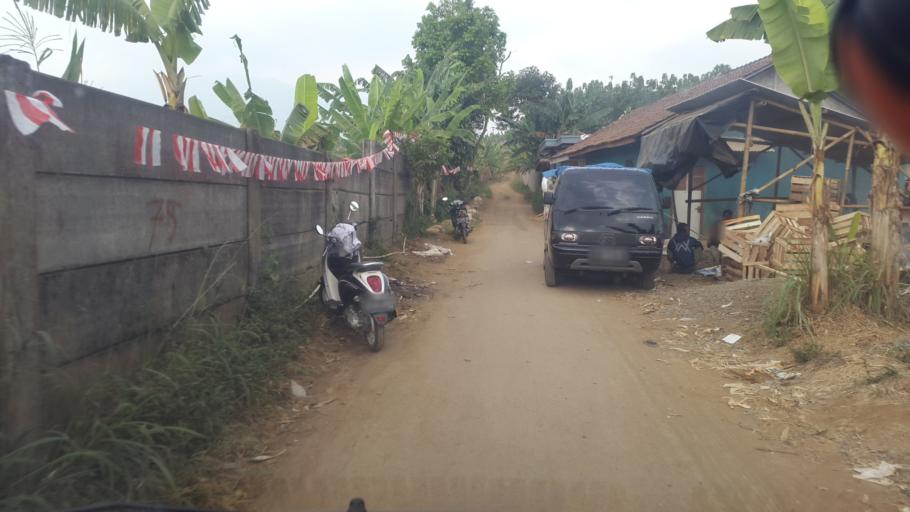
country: ID
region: West Java
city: Cicurug
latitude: -6.7684
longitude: 106.8340
